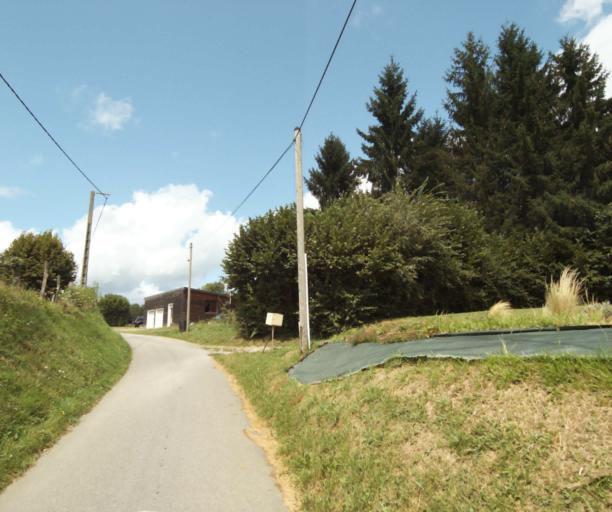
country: FR
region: Limousin
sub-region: Departement de la Correze
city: Sainte-Fortunade
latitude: 45.1918
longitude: 1.8314
